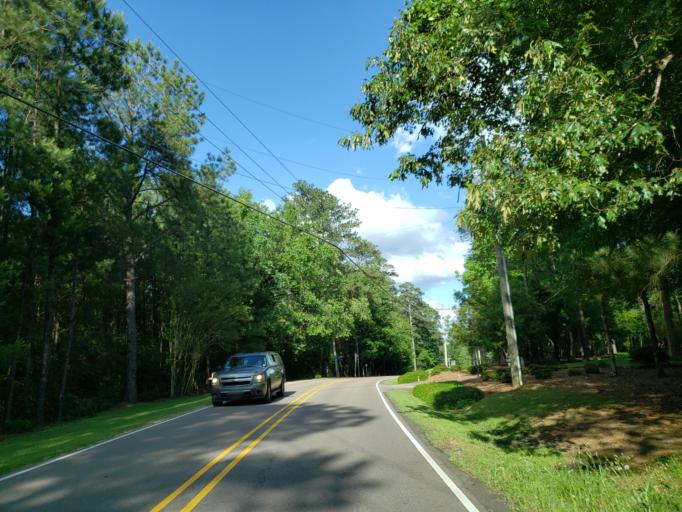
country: US
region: Mississippi
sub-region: Lamar County
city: West Hattiesburg
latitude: 31.2727
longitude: -89.4030
